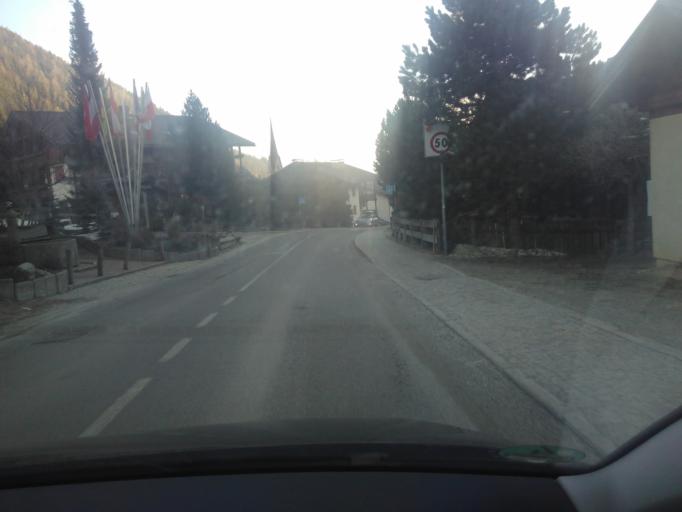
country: IT
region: Trentino-Alto Adige
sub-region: Bolzano
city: Fortezza
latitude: 46.8412
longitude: 11.6256
